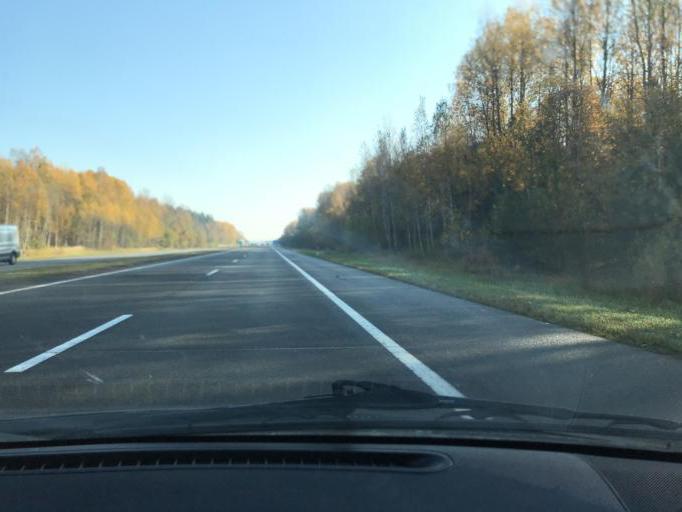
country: BY
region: Minsk
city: Bobr
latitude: 54.3718
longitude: 29.2630
